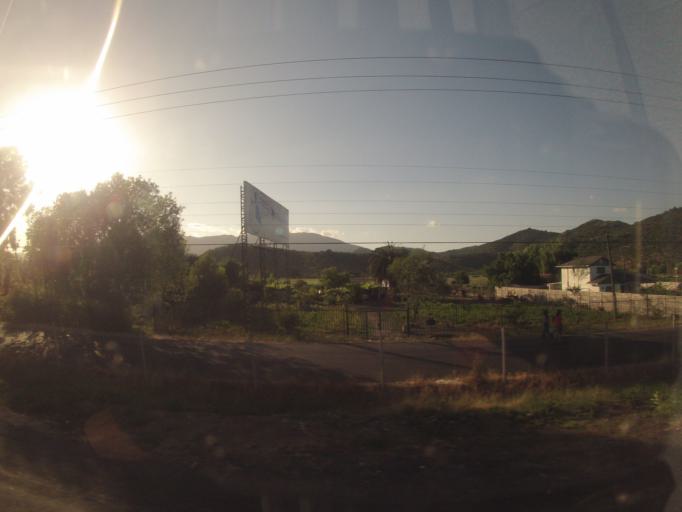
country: CL
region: O'Higgins
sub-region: Provincia de Cachapoal
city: Rengo
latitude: -34.5290
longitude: -70.9375
